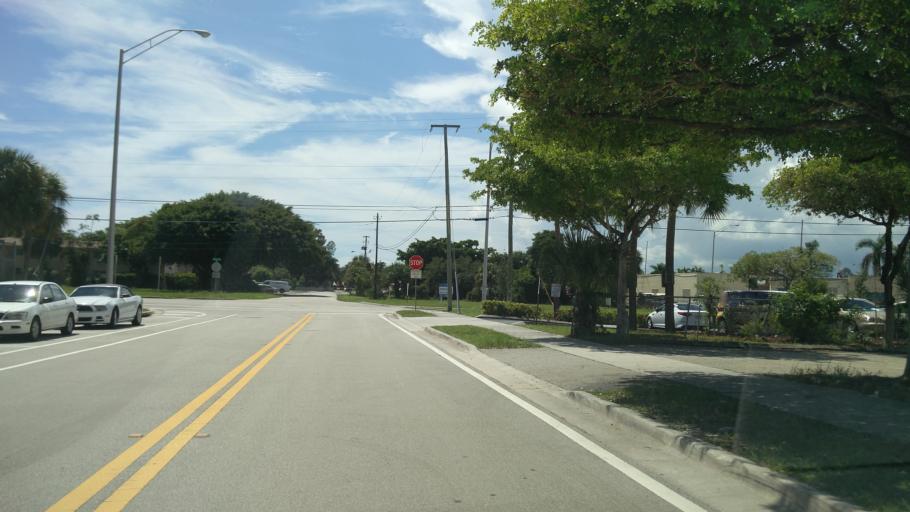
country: US
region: Florida
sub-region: Broward County
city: Terra Mar
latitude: 26.2306
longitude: -80.1019
